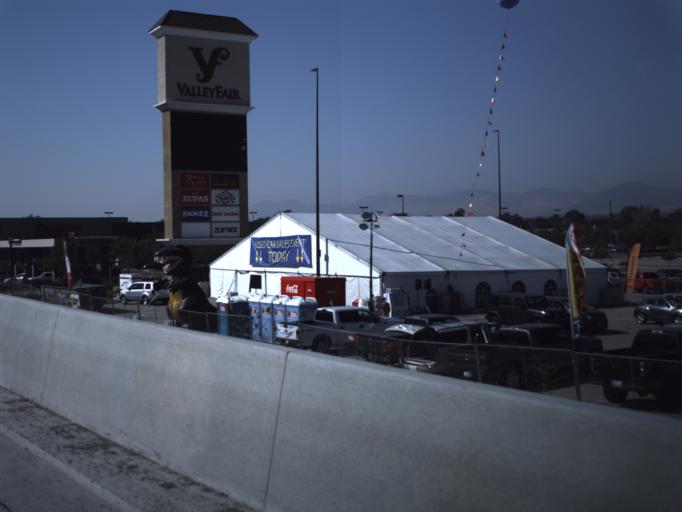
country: US
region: Utah
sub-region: Salt Lake County
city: Taylorsville
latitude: 40.6926
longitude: -111.9524
